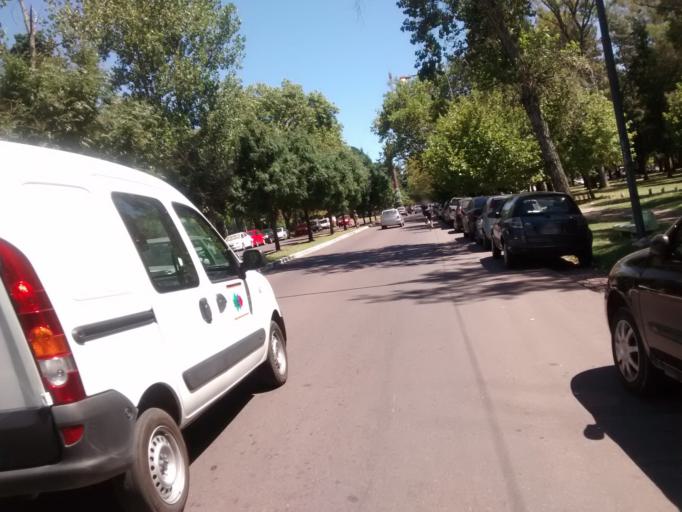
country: AR
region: Buenos Aires
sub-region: Partido de La Plata
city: La Plata
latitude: -34.9086
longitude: -57.9406
